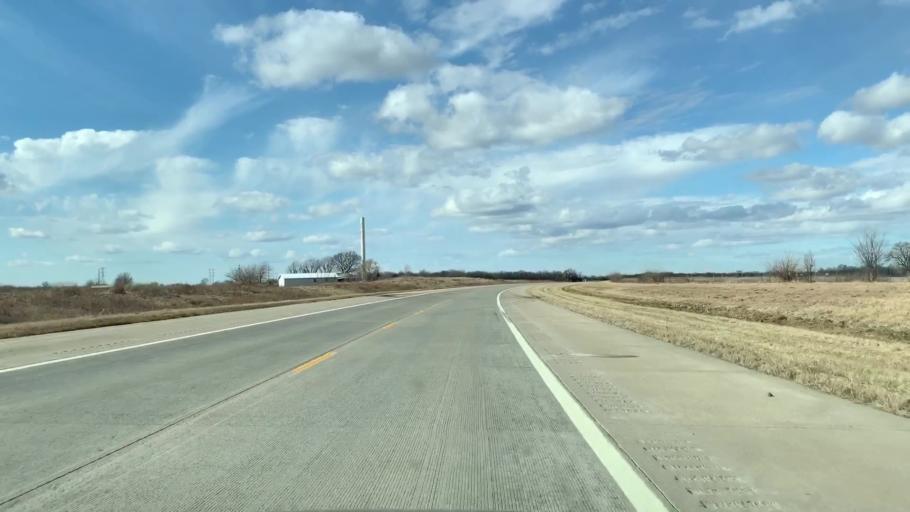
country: US
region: Kansas
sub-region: Labette County
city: Parsons
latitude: 37.3524
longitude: -95.2086
